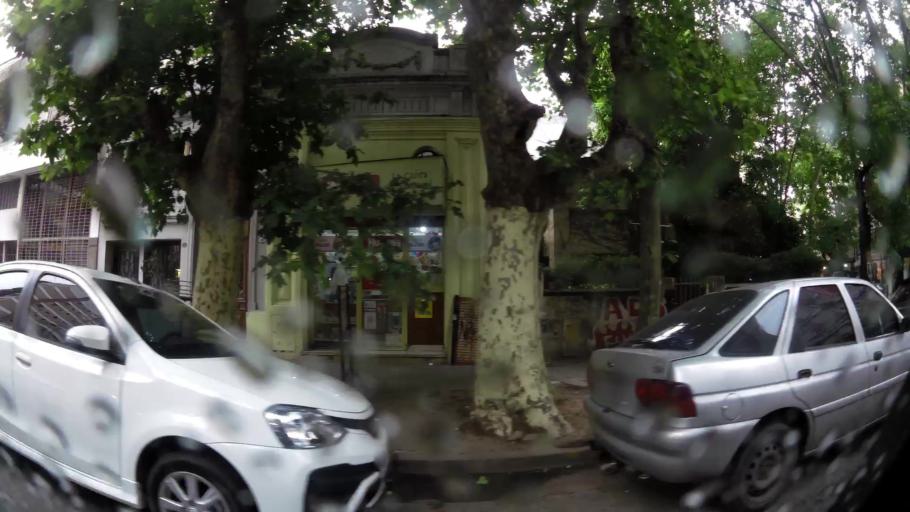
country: AR
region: Buenos Aires
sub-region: Partido de Lanus
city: Lanus
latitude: -34.7067
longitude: -58.3940
